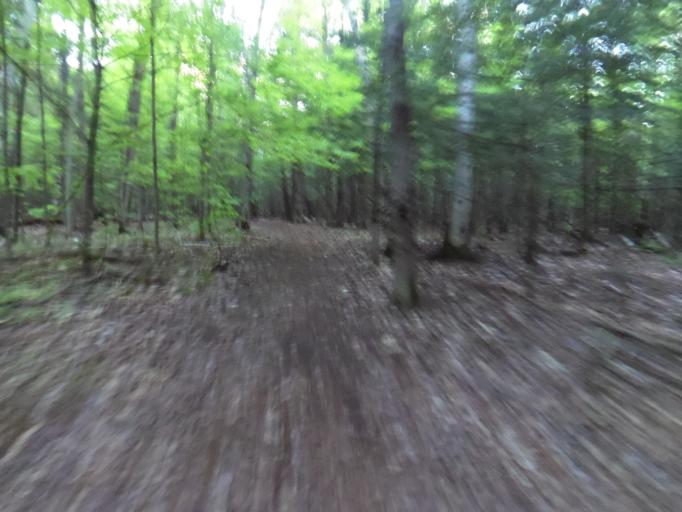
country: CA
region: Ontario
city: Bells Corners
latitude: 45.3222
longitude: -75.8131
